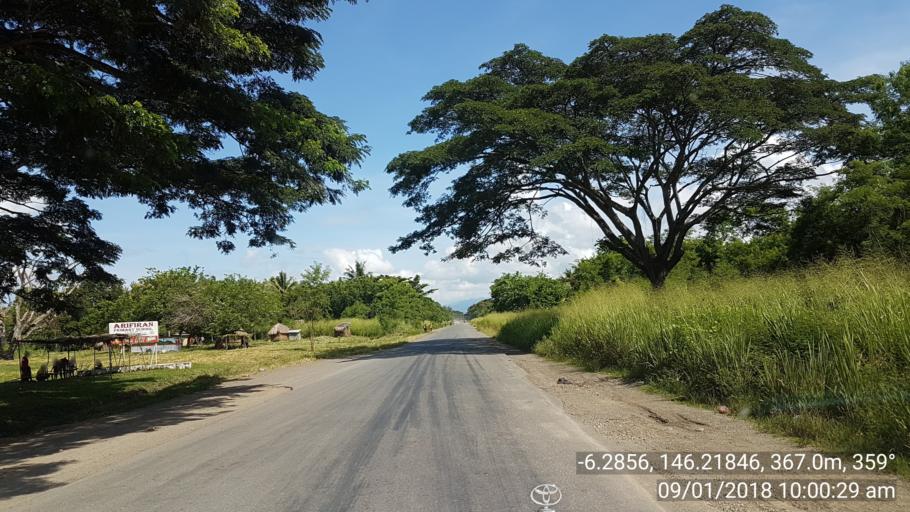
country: PG
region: Eastern Highlands
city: Kainantu
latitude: -6.2857
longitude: 146.2184
